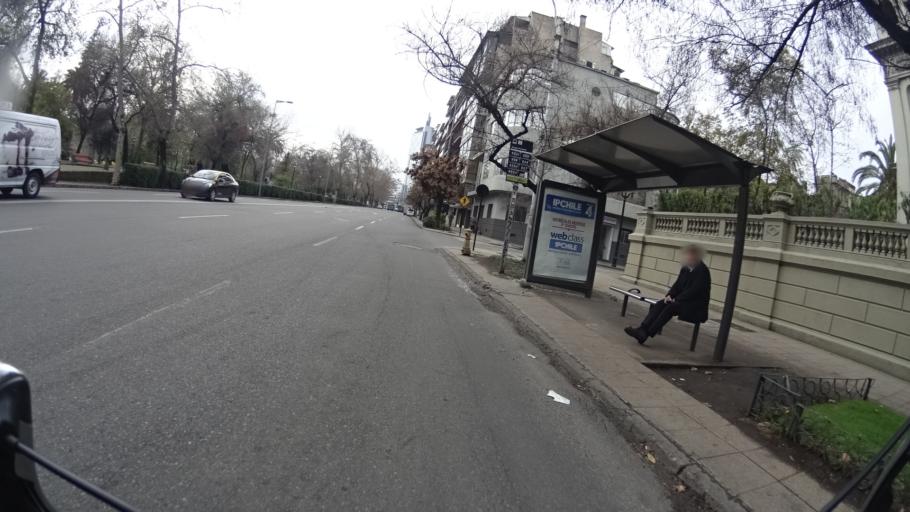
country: CL
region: Santiago Metropolitan
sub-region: Provincia de Santiago
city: Santiago
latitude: -33.4368
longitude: -70.6392
